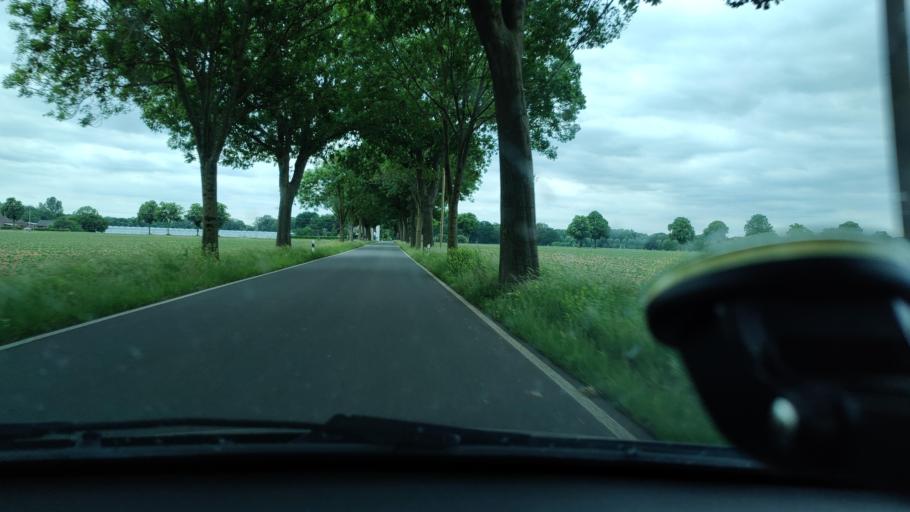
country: DE
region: North Rhine-Westphalia
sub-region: Regierungsbezirk Dusseldorf
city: Goch
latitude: 51.6804
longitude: 6.1055
